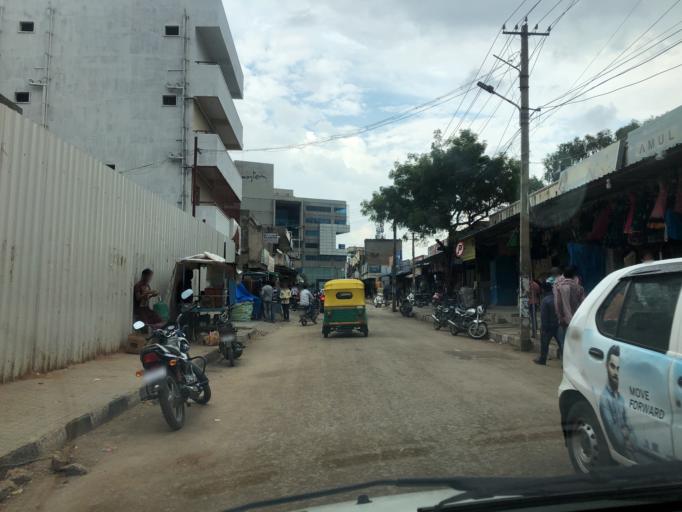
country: IN
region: Karnataka
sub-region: Bangalore Urban
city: Bangalore
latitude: 12.9927
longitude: 77.7011
